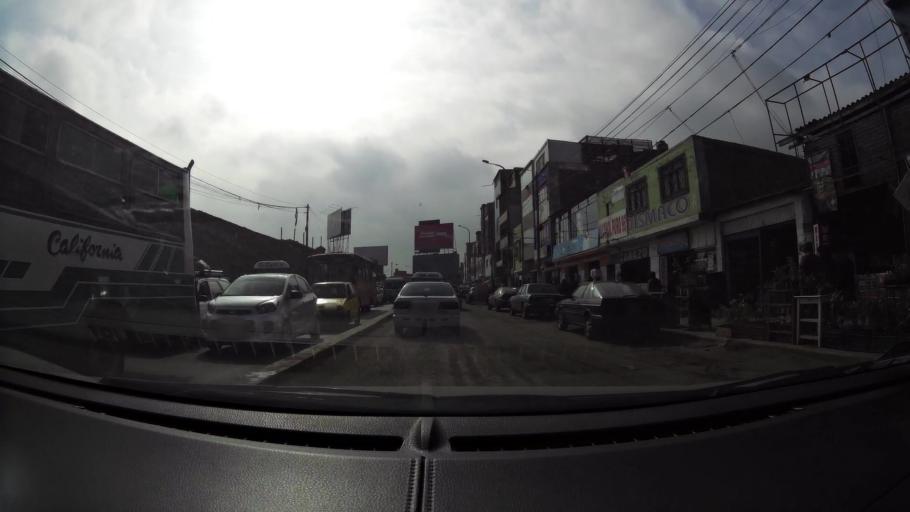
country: PE
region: La Libertad
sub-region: Provincia de Trujillo
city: Trujillo
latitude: -8.1098
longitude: -79.0204
